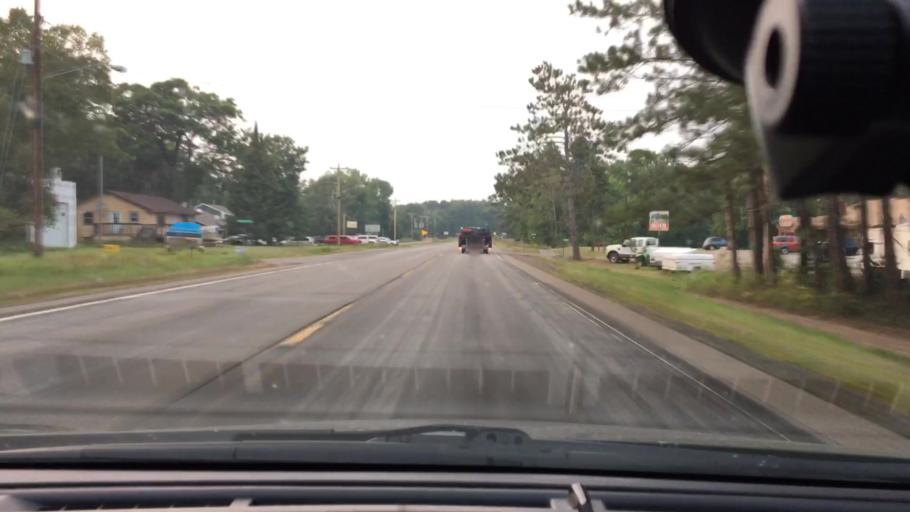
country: US
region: Minnesota
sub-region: Crow Wing County
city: Cross Lake
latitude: 46.7876
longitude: -93.9662
